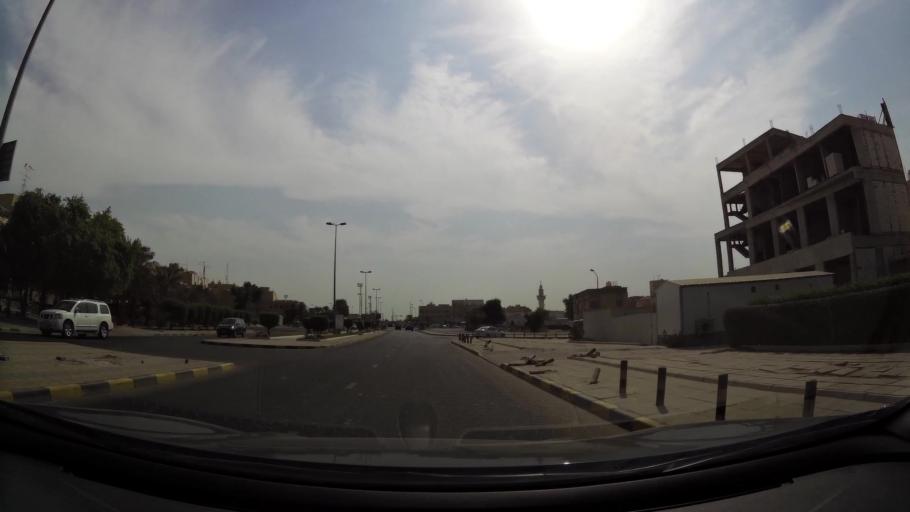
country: KW
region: Al Asimah
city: Ash Shamiyah
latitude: 29.3464
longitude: 47.9677
